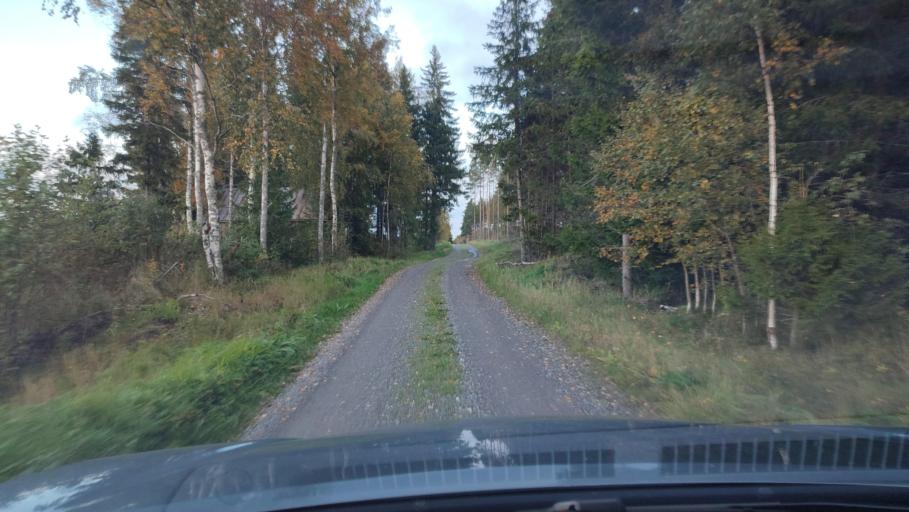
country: FI
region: Ostrobothnia
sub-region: Sydosterbotten
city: Kristinestad
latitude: 62.2463
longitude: 21.4530
